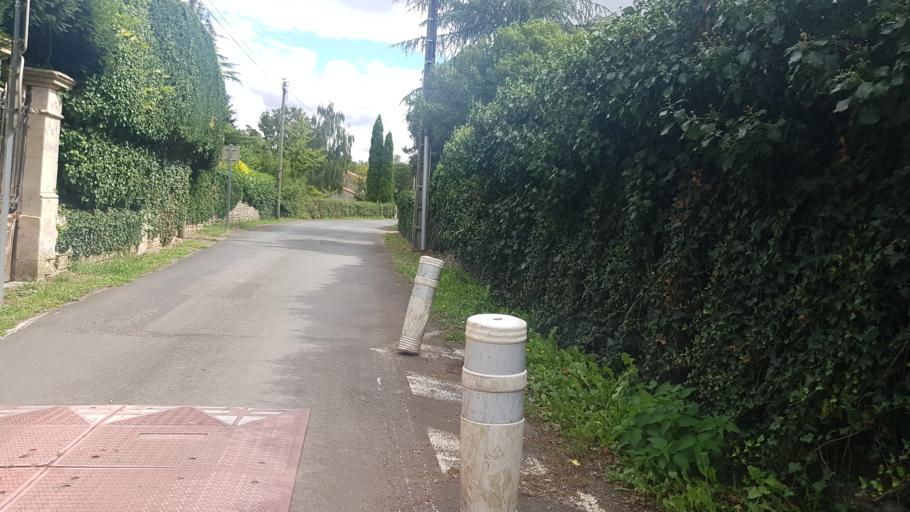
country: FR
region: Poitou-Charentes
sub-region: Departement des Deux-Sevres
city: Vouille
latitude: 46.3279
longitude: -0.3441
